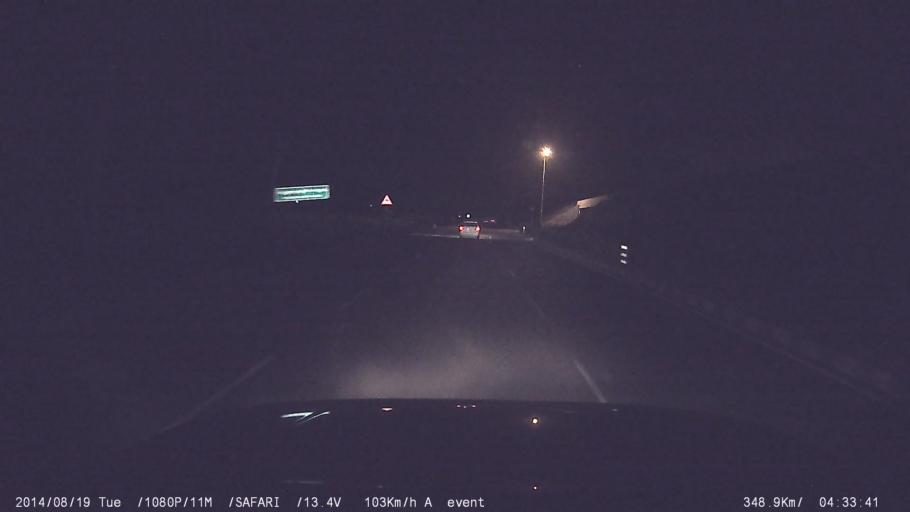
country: IN
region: Tamil Nadu
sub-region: Erode
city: Perundurai
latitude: 11.2969
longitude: 77.5956
